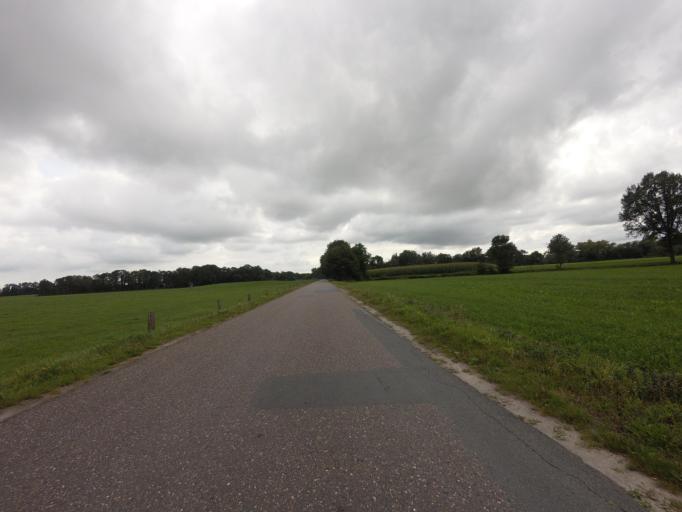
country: NL
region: Overijssel
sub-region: Gemeente Losser
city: Losser
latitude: 52.2571
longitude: 7.0259
